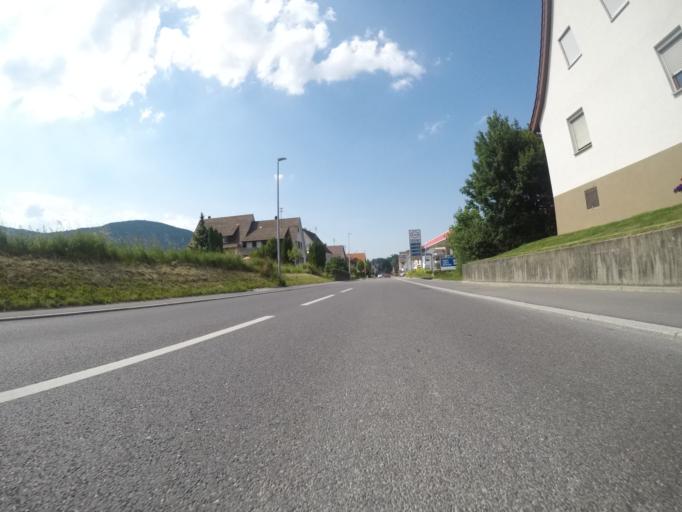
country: DE
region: Baden-Wuerttemberg
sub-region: Regierungsbezirk Stuttgart
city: Owen
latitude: 48.5591
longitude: 9.4659
